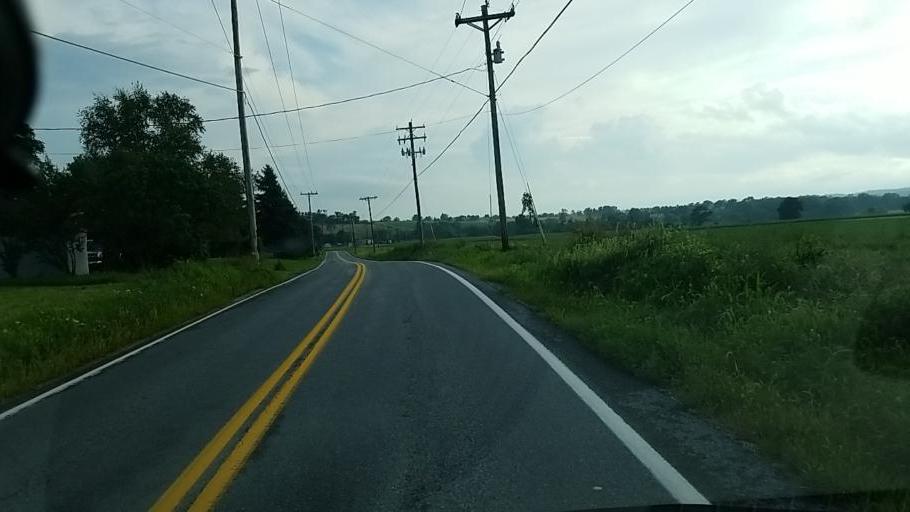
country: US
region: Pennsylvania
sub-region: Cumberland County
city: Newville
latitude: 40.2202
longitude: -77.4623
